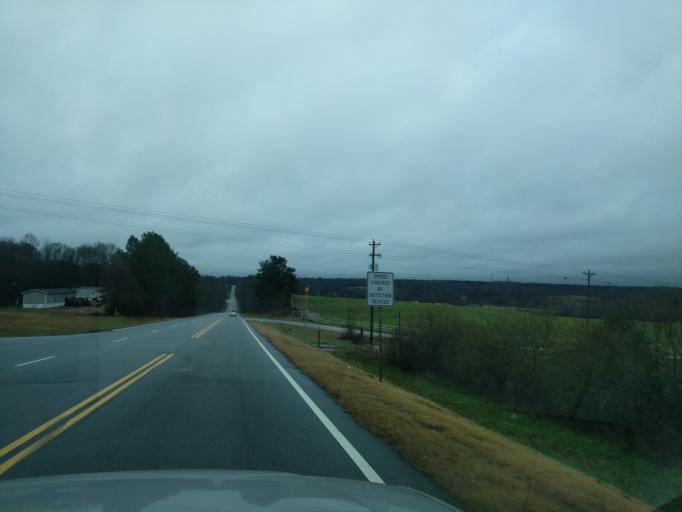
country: US
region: Georgia
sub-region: Franklin County
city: Lavonia
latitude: 34.3890
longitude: -83.0991
